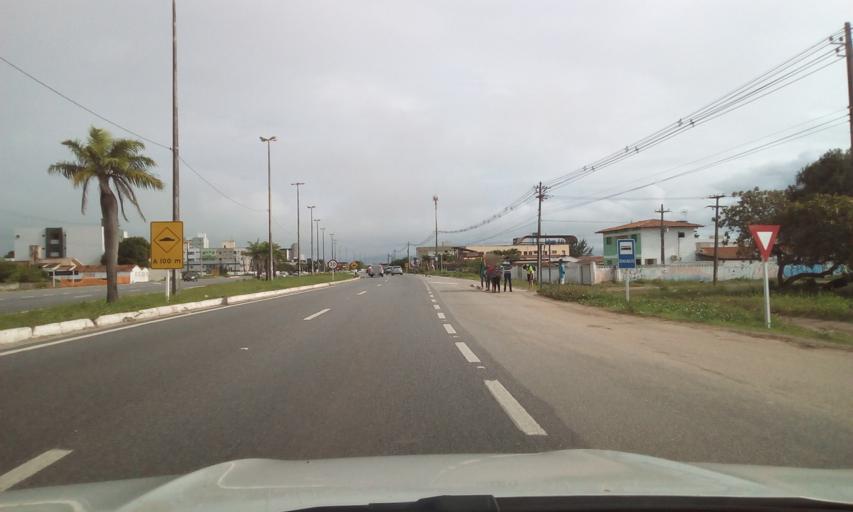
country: BR
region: Paraiba
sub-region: Cabedelo
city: Cabedelo
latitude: -7.0042
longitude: -34.8290
